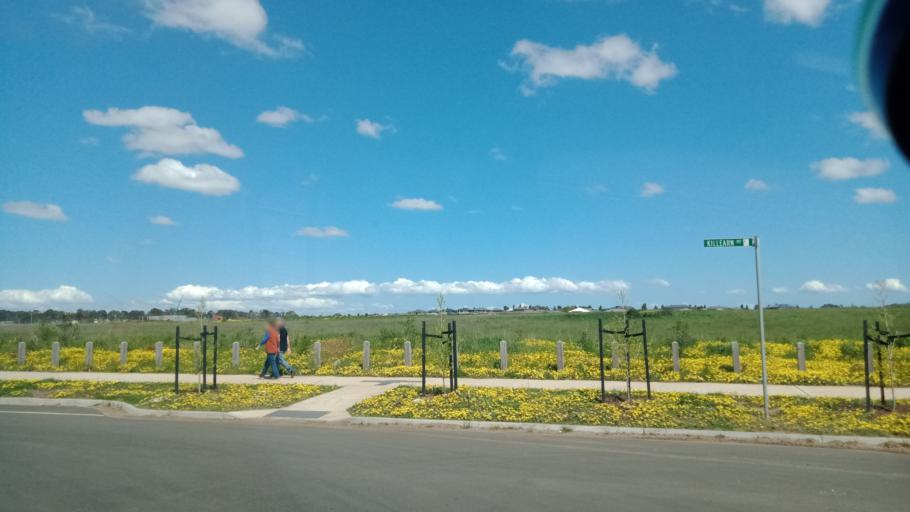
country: AU
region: Victoria
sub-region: Casey
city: Cranbourne West
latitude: -38.1025
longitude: 145.2463
